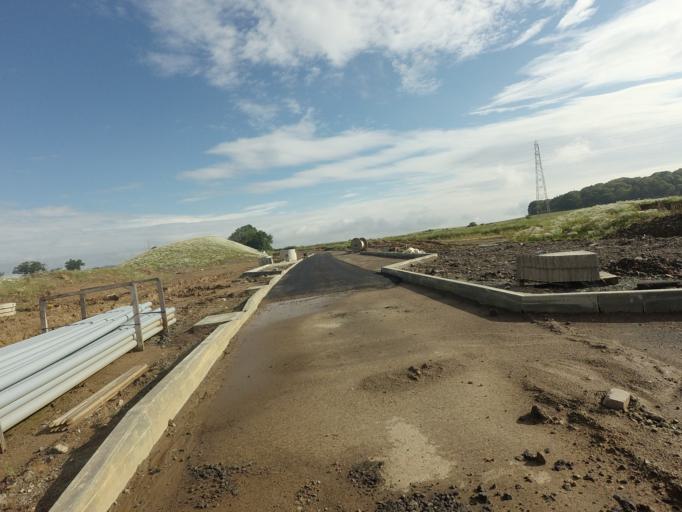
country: GB
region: Scotland
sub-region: West Lothian
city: Kirknewton
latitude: 55.9034
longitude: -3.4356
